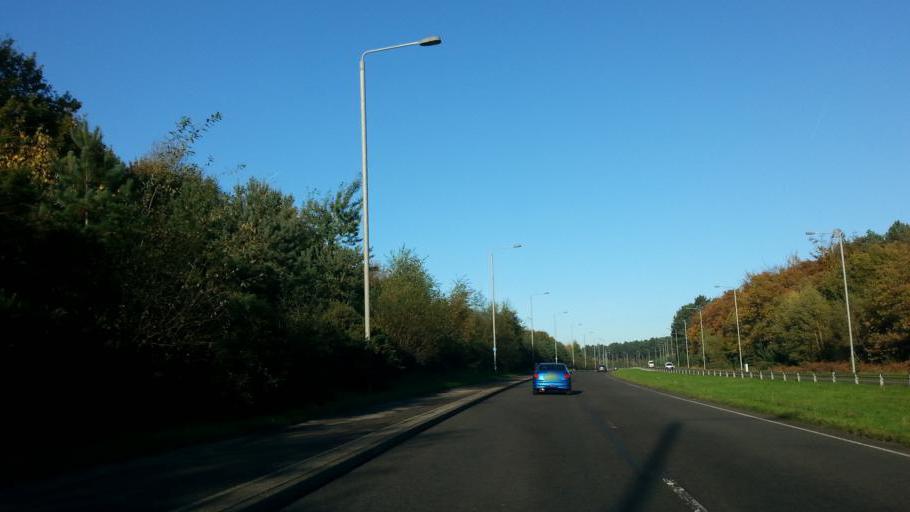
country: GB
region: England
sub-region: Nottinghamshire
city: Rainworth
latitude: 53.1245
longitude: -1.1218
